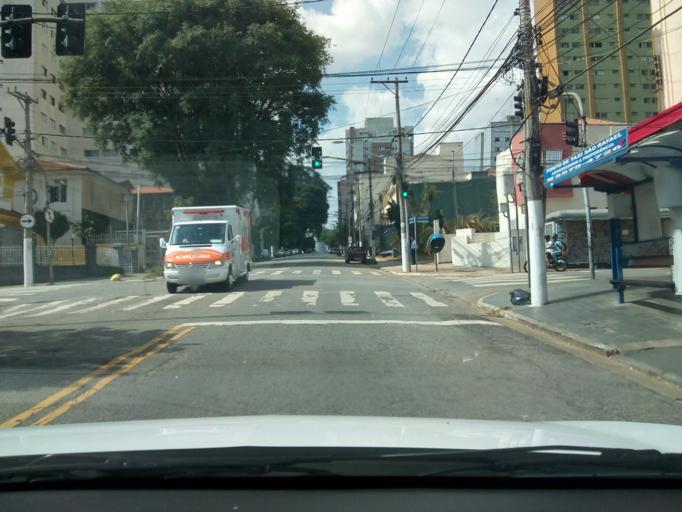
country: BR
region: Sao Paulo
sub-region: Sao Paulo
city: Sao Paulo
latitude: -23.5794
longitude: -46.6445
